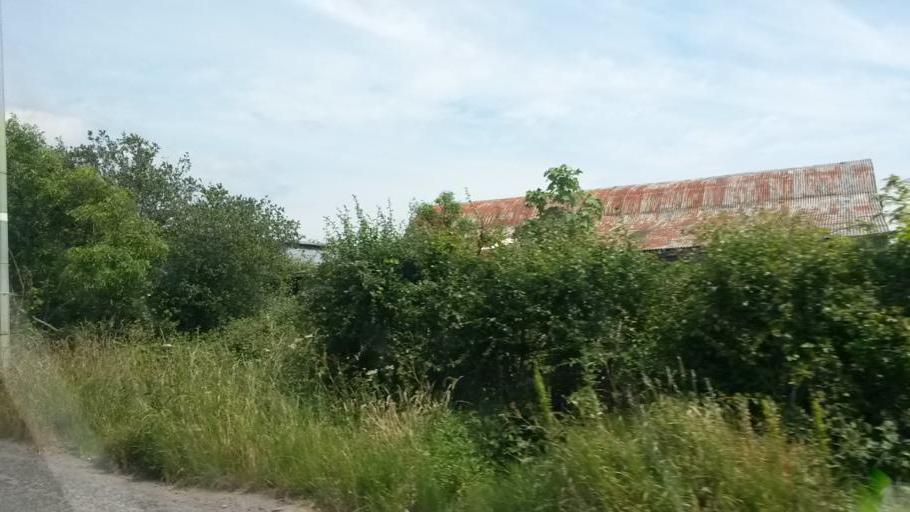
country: IE
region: Leinster
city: Balrothery
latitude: 53.5609
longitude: -6.2101
